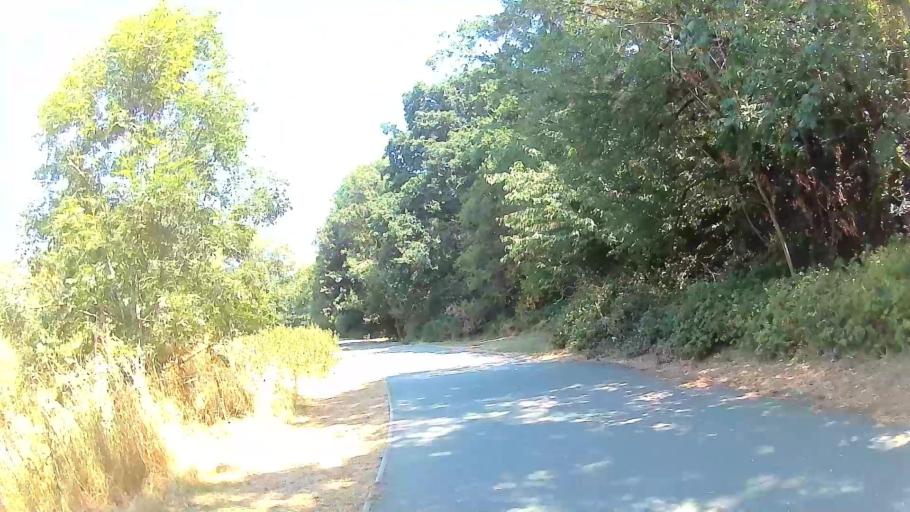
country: GB
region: England
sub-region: Greater London
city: Hornchurch
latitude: 51.5517
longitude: 0.2358
